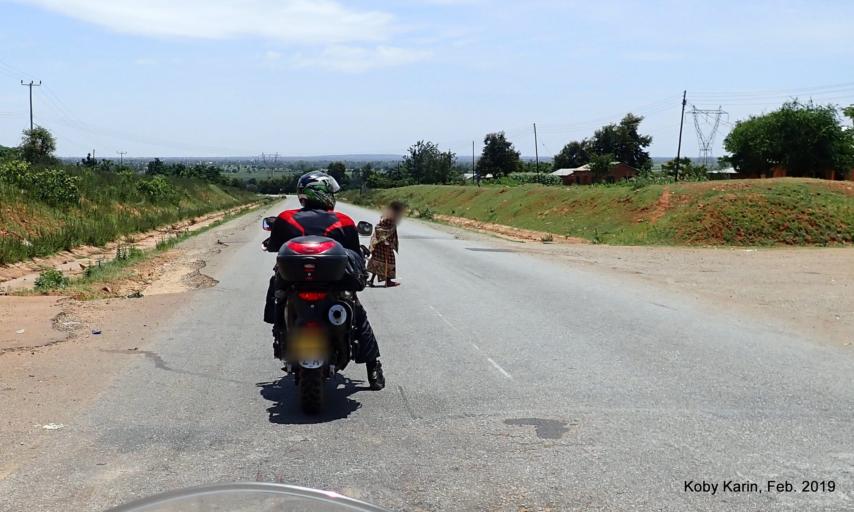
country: TZ
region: Singida
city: Kiomboi
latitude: -4.4103
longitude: 34.3753
